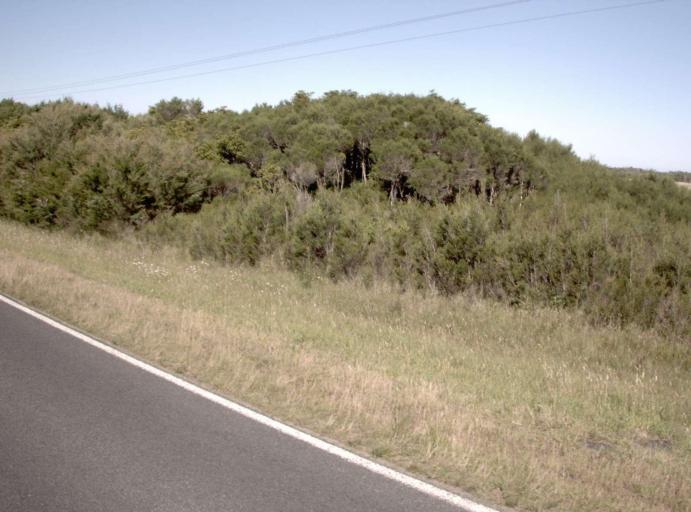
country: AU
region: Victoria
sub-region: Latrobe
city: Morwell
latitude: -38.6547
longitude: 146.4610
